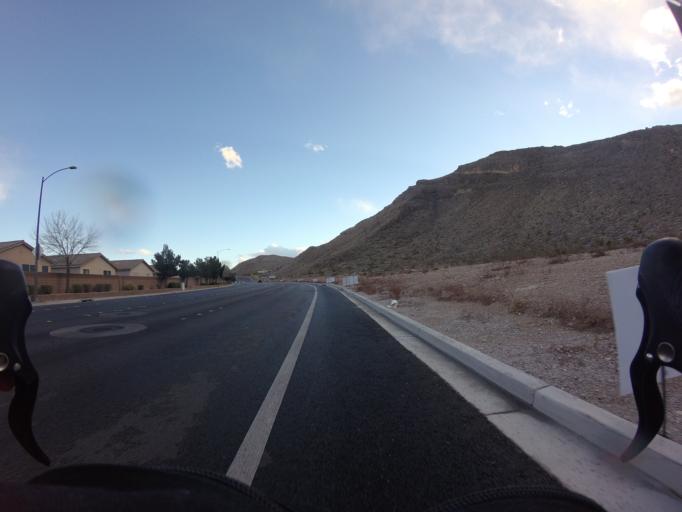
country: US
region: Nevada
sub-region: Clark County
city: Summerlin South
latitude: 36.2289
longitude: -115.3320
